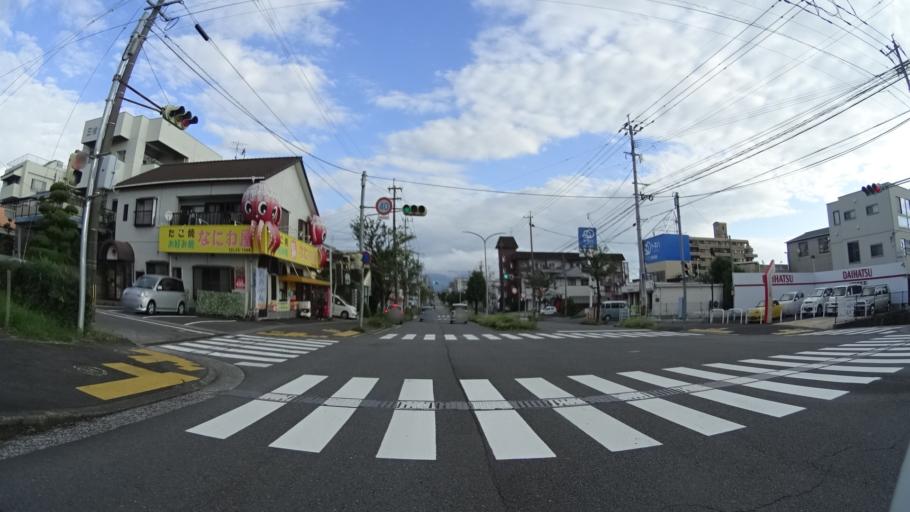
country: JP
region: Oita
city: Beppu
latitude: 33.2885
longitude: 131.4962
